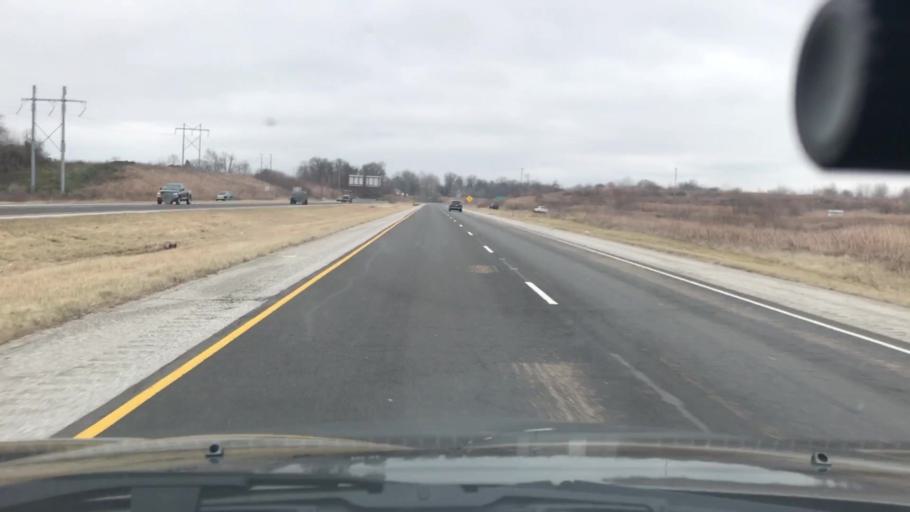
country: US
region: Illinois
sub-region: Madison County
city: Roxana
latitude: 38.8695
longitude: -90.0586
